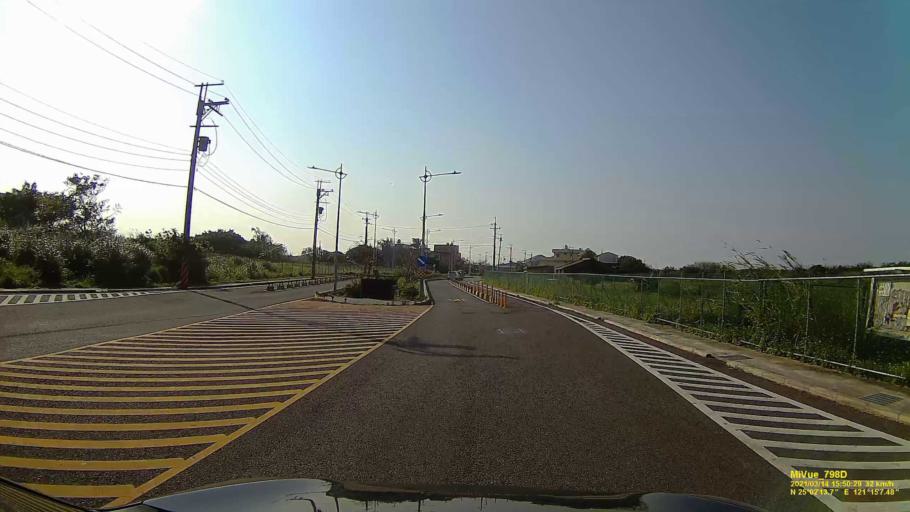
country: TW
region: Taiwan
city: Taoyuan City
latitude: 25.0372
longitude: 121.2518
